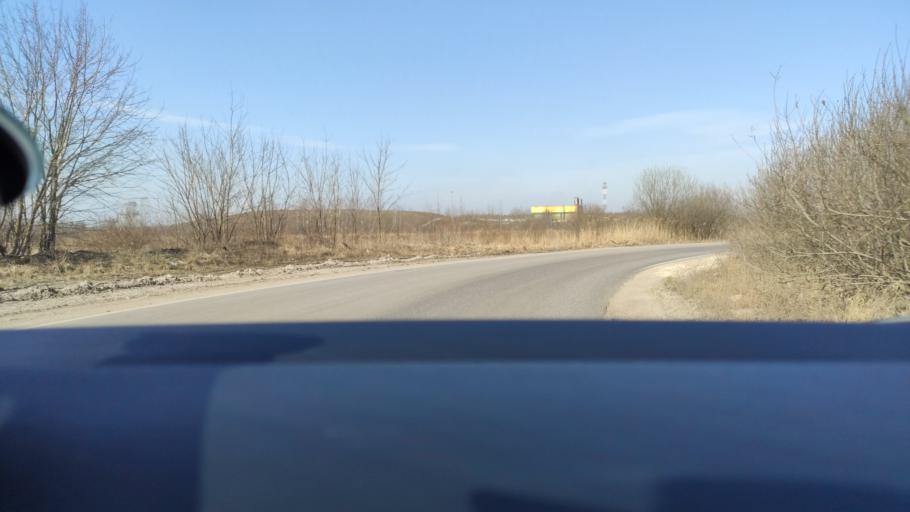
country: RU
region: Moskovskaya
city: Elektrostal'
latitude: 55.7642
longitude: 38.3878
